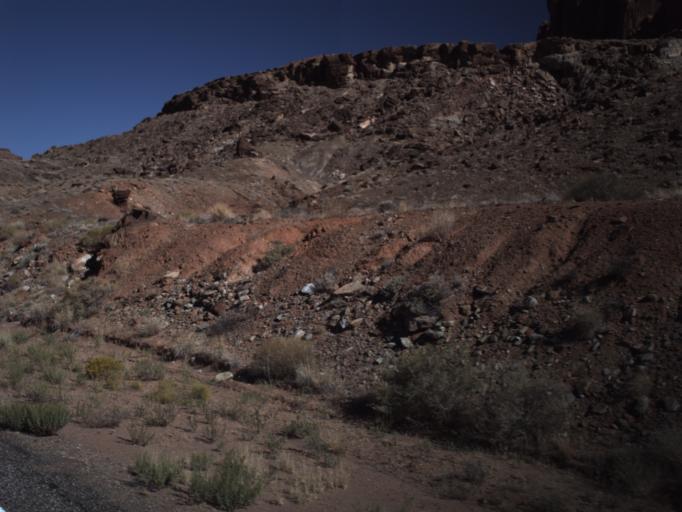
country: US
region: Utah
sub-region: San Juan County
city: Blanding
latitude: 37.9172
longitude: -110.4618
